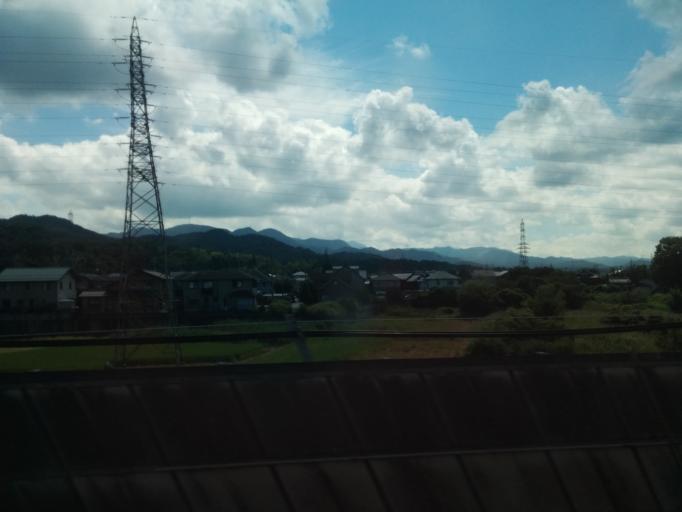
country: JP
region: Shiga Prefecture
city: Hikone
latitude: 35.2504
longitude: 136.2725
